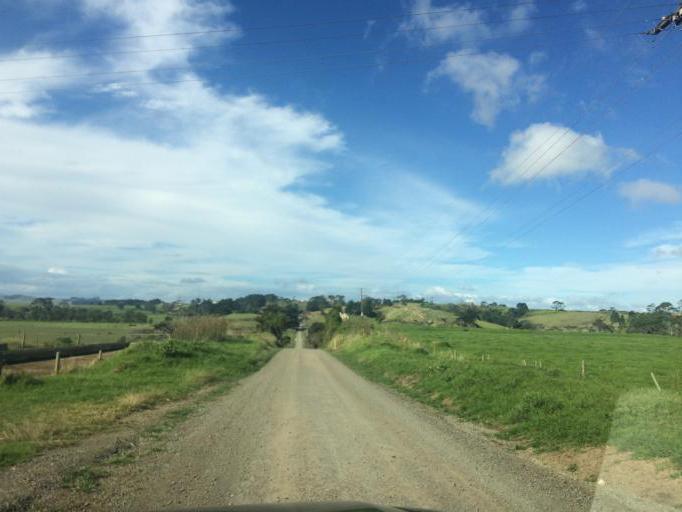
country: NZ
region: Northland
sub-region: Kaipara District
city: Dargaville
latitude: -36.0282
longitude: 173.8673
